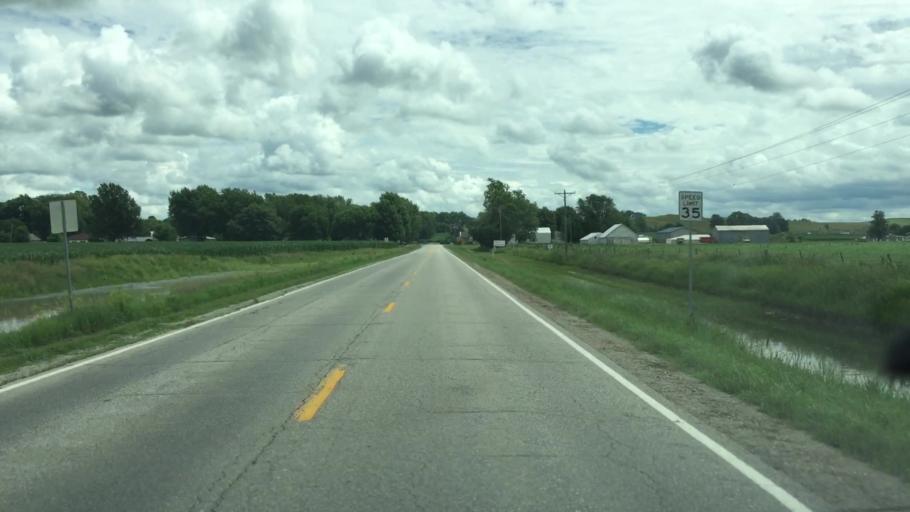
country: US
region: Iowa
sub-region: Jasper County
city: Monroe
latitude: 41.5770
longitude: -93.0288
